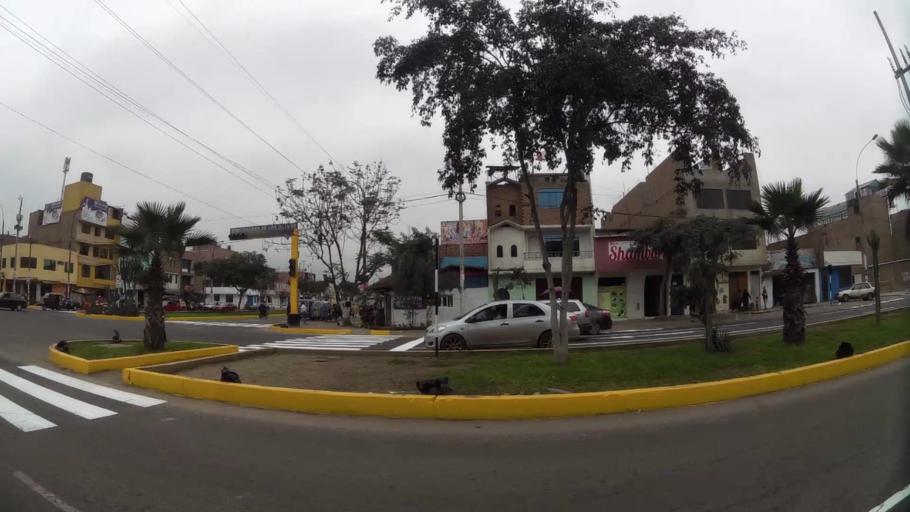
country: PE
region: Lima
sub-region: Lima
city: Independencia
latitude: -11.9702
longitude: -77.0804
